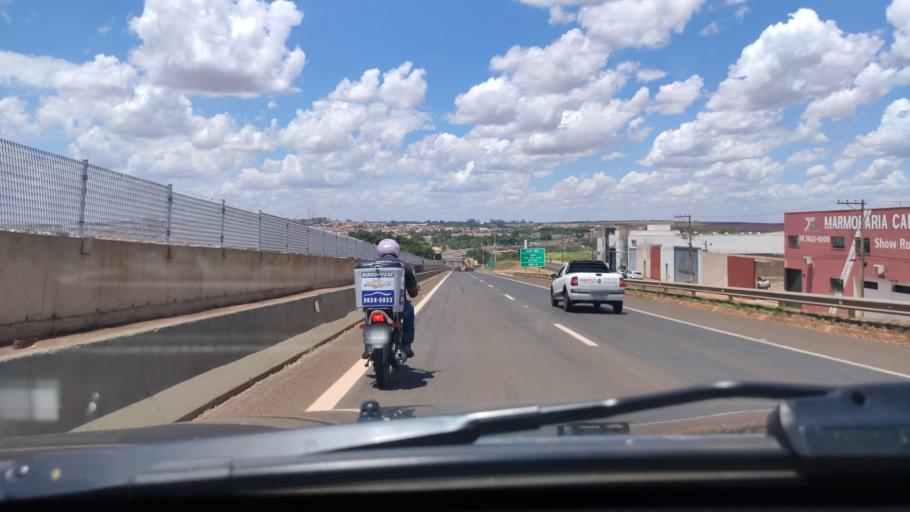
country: BR
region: Sao Paulo
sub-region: Jau
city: Jau
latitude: -22.2721
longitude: -48.5619
